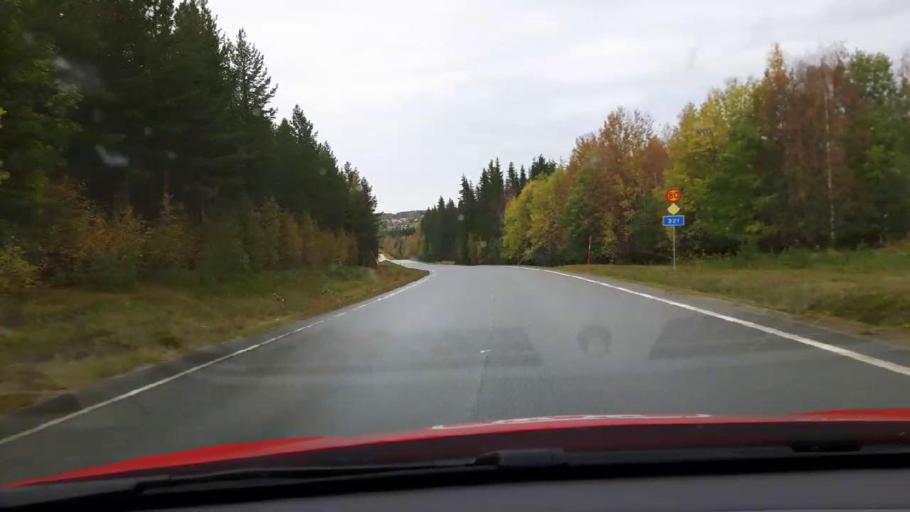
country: SE
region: Jaemtland
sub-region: Bergs Kommun
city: Hoverberg
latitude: 62.9233
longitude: 14.3354
